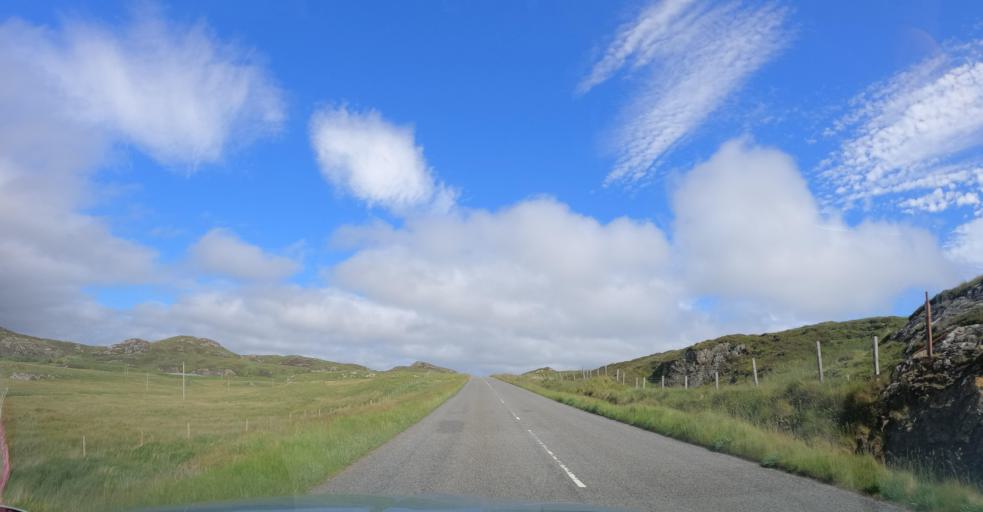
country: GB
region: Scotland
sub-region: Eilean Siar
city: Stornoway
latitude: 58.1058
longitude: -6.5443
